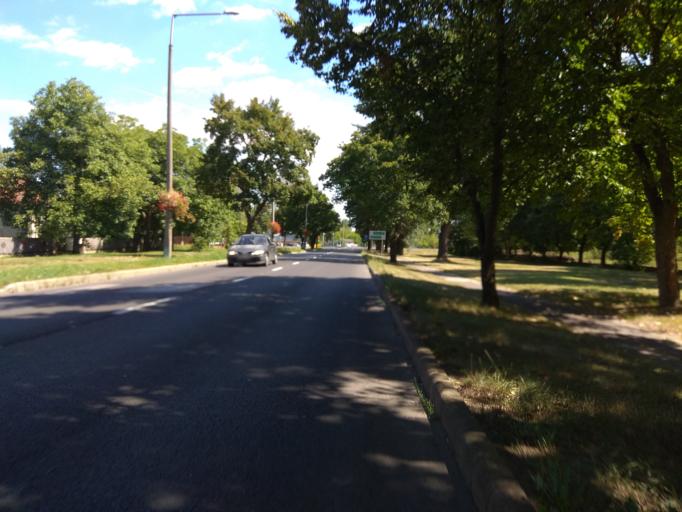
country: HU
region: Borsod-Abauj-Zemplen
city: Kazincbarcika
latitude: 48.2529
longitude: 20.6420
